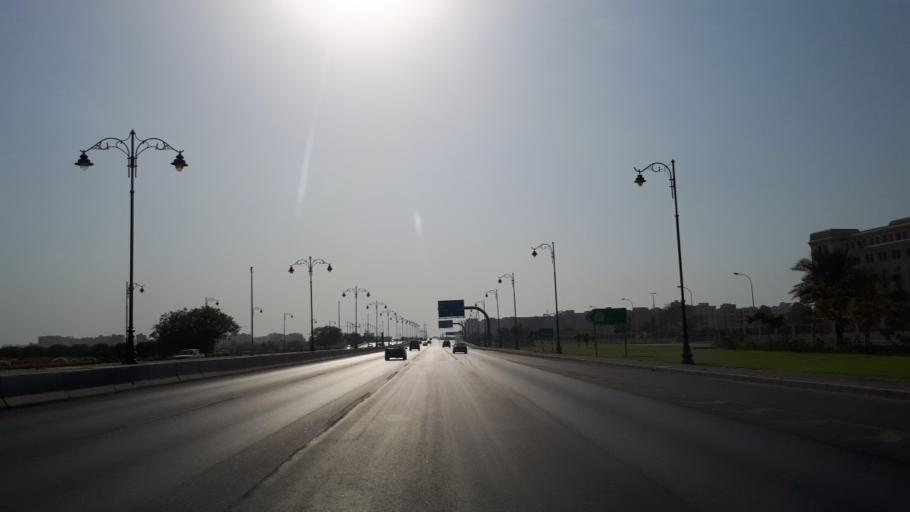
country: OM
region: Muhafazat Masqat
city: Bawshar
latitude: 23.5855
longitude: 58.3911
